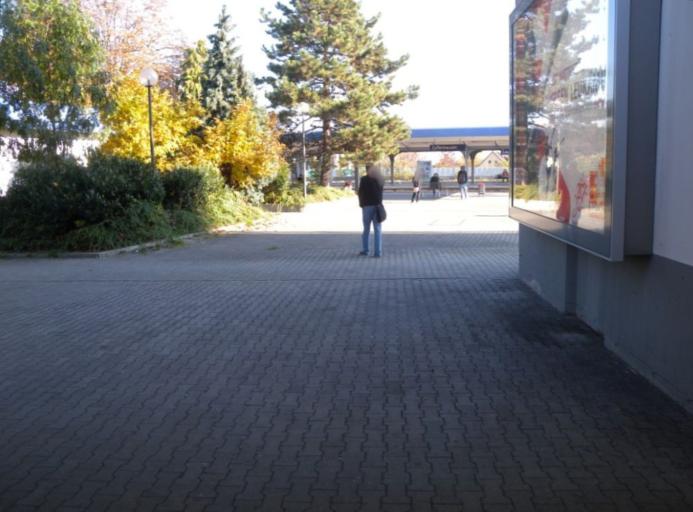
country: DE
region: Baden-Wuerttemberg
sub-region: Regierungsbezirk Stuttgart
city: Stuttgart Feuerbach
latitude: 48.8292
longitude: 9.1667
